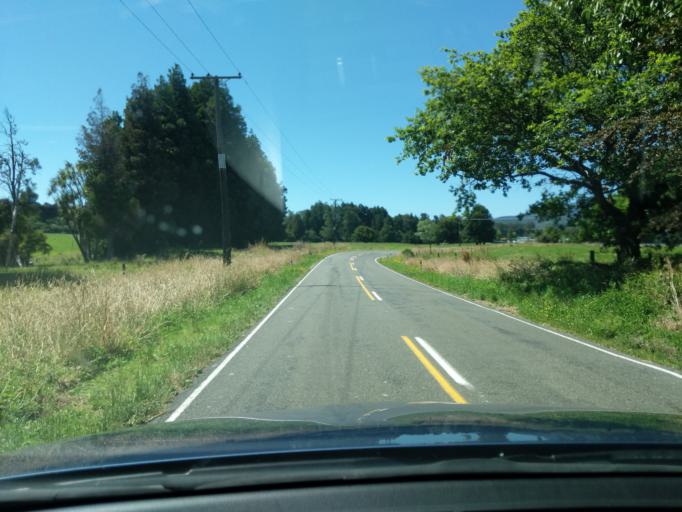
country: NZ
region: Tasman
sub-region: Tasman District
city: Takaka
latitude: -40.7037
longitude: 172.6352
